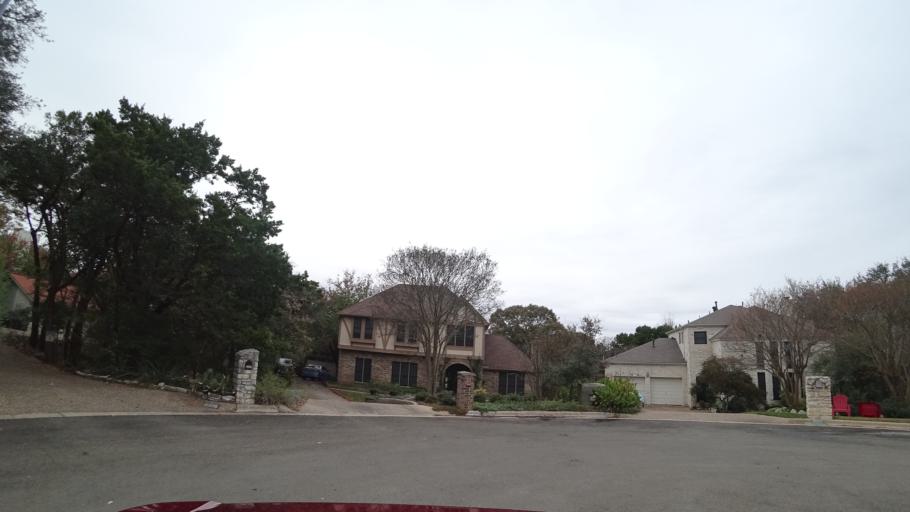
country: US
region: Texas
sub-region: Williamson County
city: Jollyville
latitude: 30.3763
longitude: -97.7936
